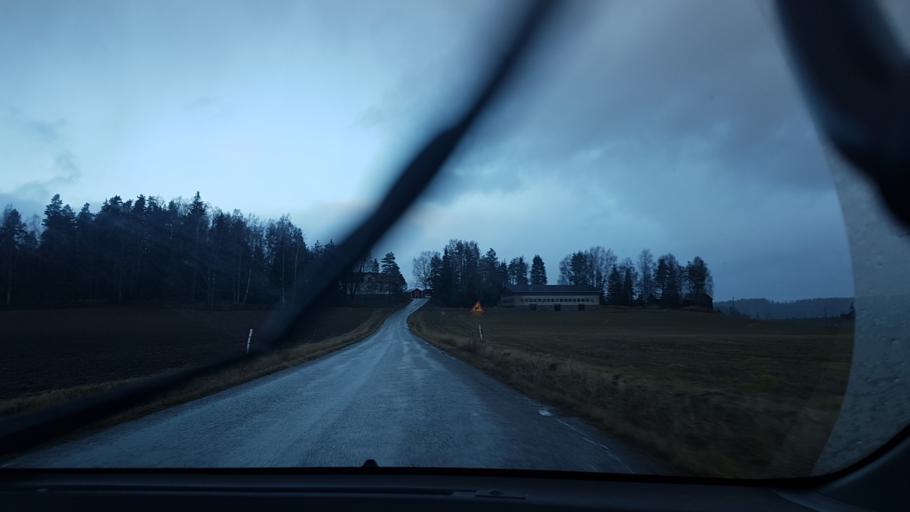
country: FI
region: Uusimaa
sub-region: Helsinki
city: Lohja
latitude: 60.2098
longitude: 24.1009
